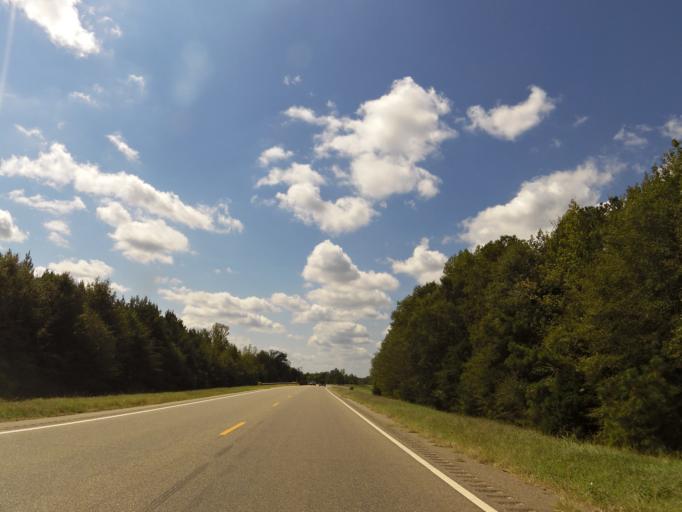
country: US
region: Alabama
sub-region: Dallas County
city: Selma
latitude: 32.3686
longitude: -87.1084
